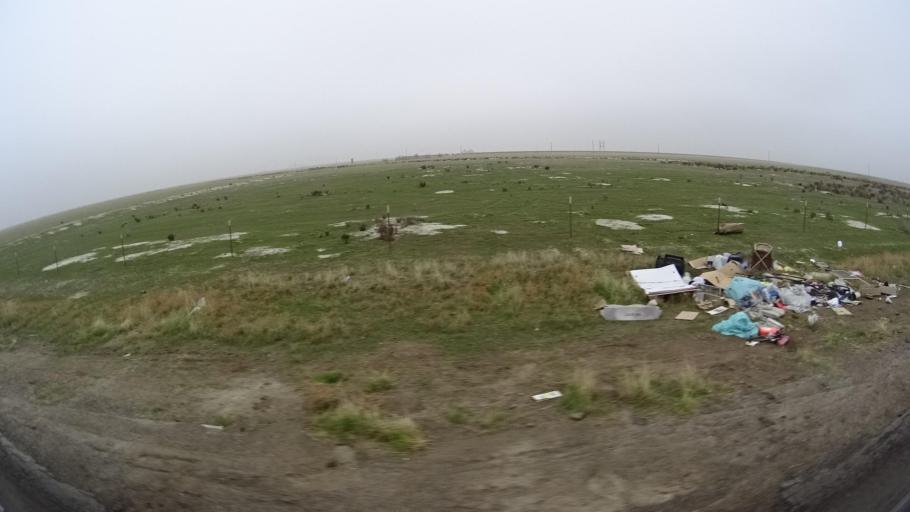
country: US
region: California
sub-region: Tulare County
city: Alpaugh
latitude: 35.7713
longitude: -119.4724
